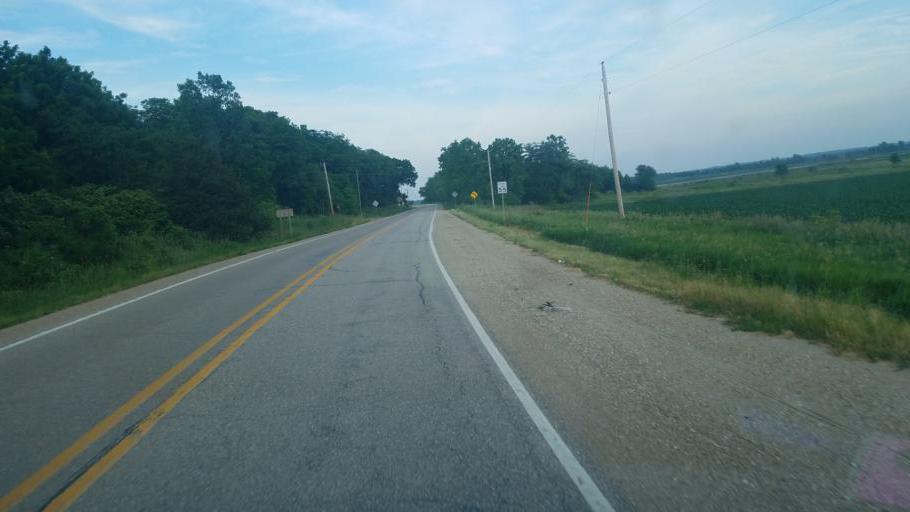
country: US
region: Iowa
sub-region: Tama County
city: Tama
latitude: 41.9634
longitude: -92.4557
